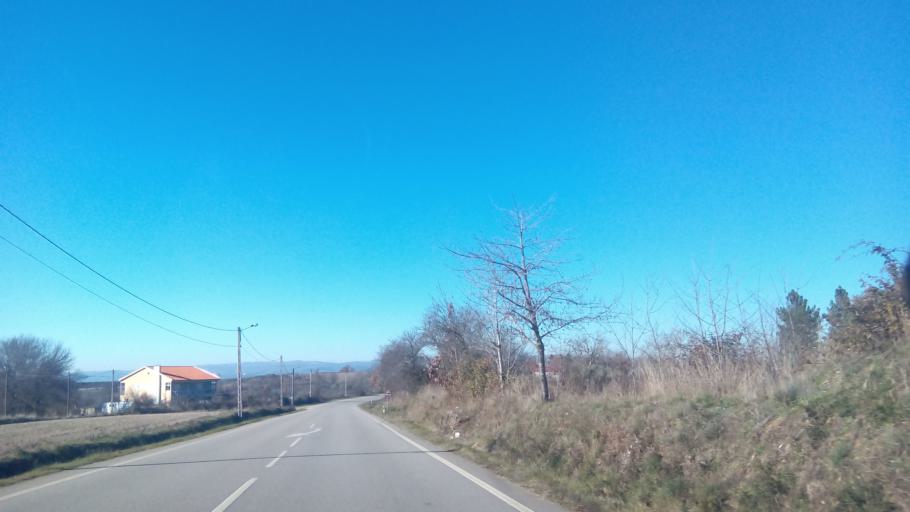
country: PT
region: Braganca
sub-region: Vimioso
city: Vimioso
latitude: 41.6011
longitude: -6.6004
